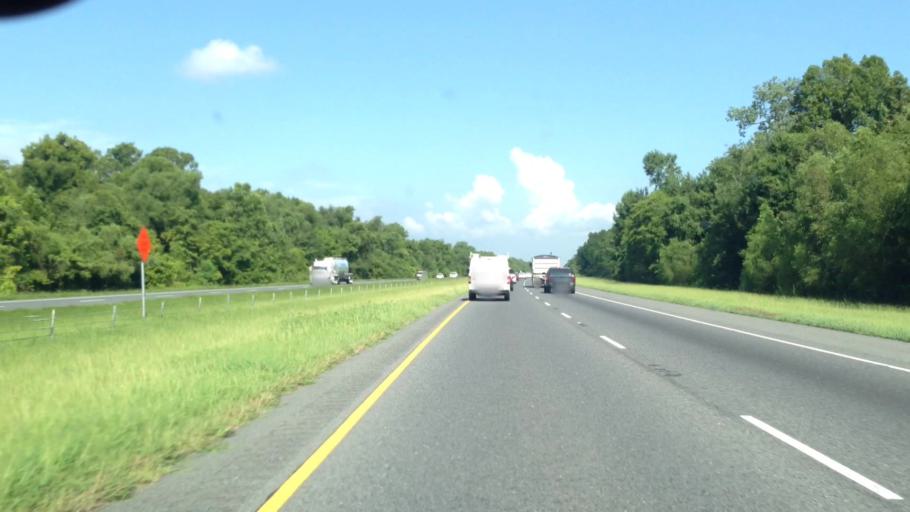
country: US
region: Louisiana
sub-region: Ascension Parish
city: Sorrento
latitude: 30.1554
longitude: -90.8174
